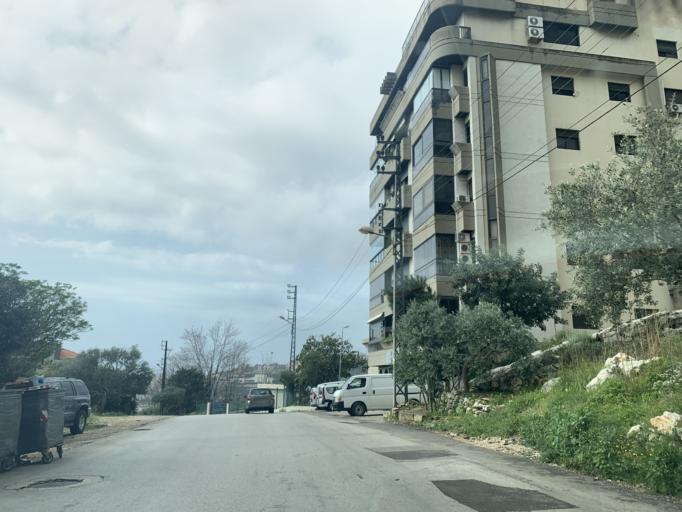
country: LB
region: Mont-Liban
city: Djounie
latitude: 34.0037
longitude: 35.6512
